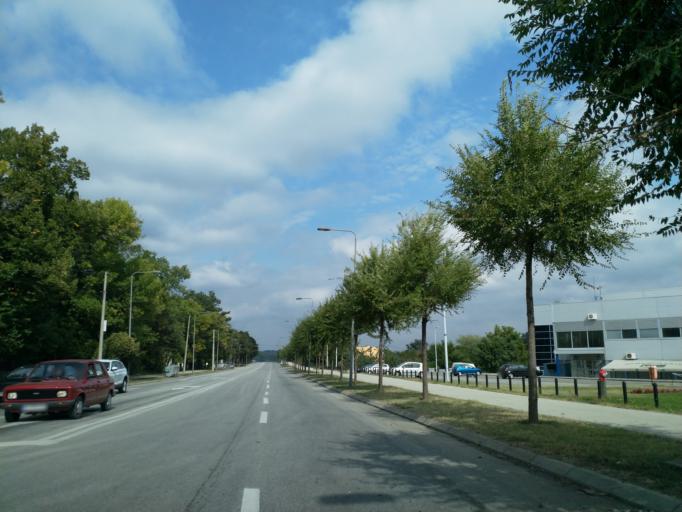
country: RS
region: Central Serbia
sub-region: Sumadijski Okrug
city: Kragujevac
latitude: 44.0247
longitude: 20.9285
